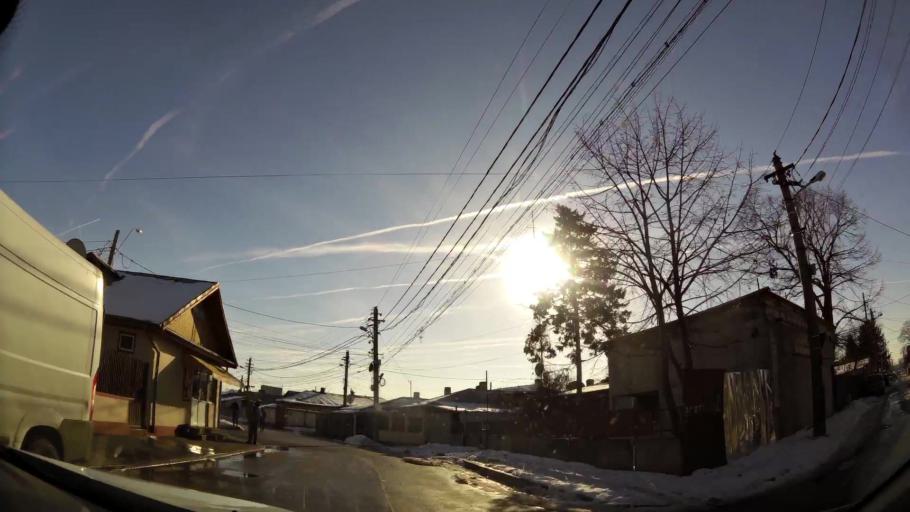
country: RO
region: Ilfov
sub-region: Voluntari City
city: Voluntari
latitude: 44.4824
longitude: 26.1427
